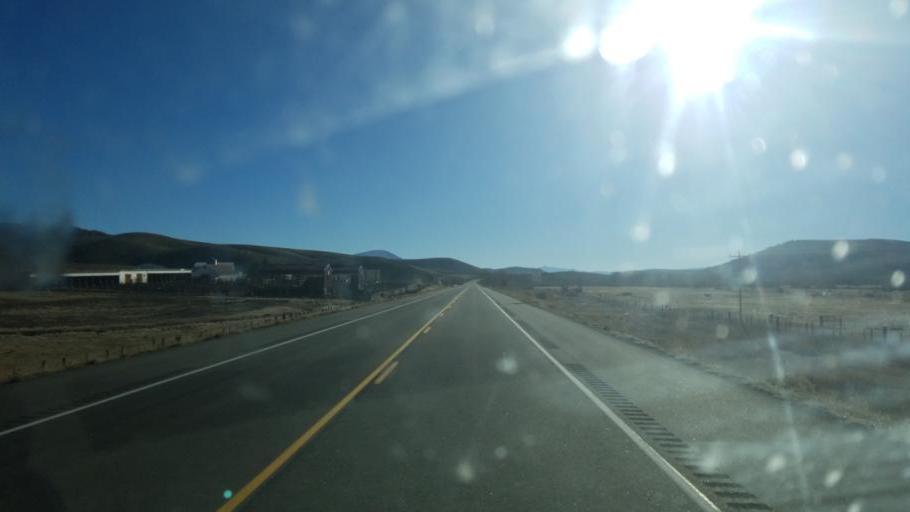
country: US
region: Colorado
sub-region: Gunnison County
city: Gunnison
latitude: 38.5227
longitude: -106.7831
